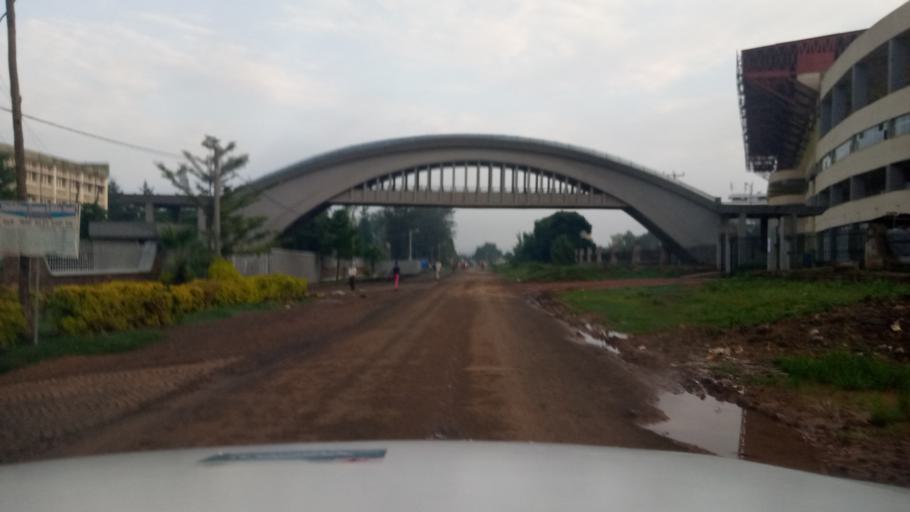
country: ET
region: Oromiya
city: Jima
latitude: 7.6761
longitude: 36.8524
